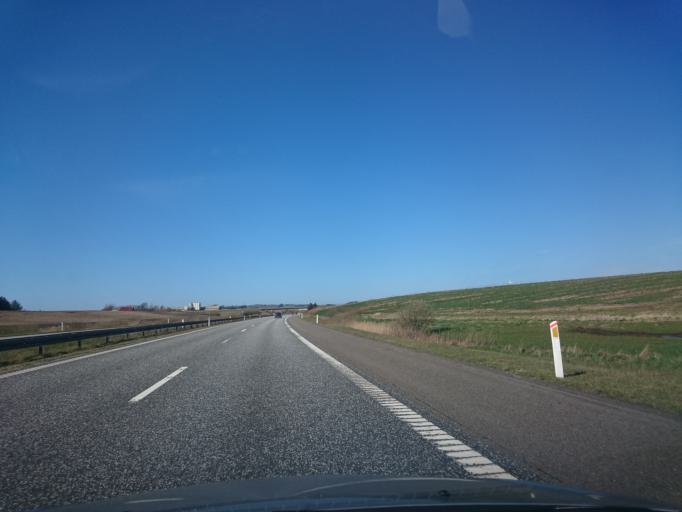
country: DK
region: North Denmark
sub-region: Hjorring Kommune
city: Hirtshals
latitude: 57.5389
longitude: 10.0075
